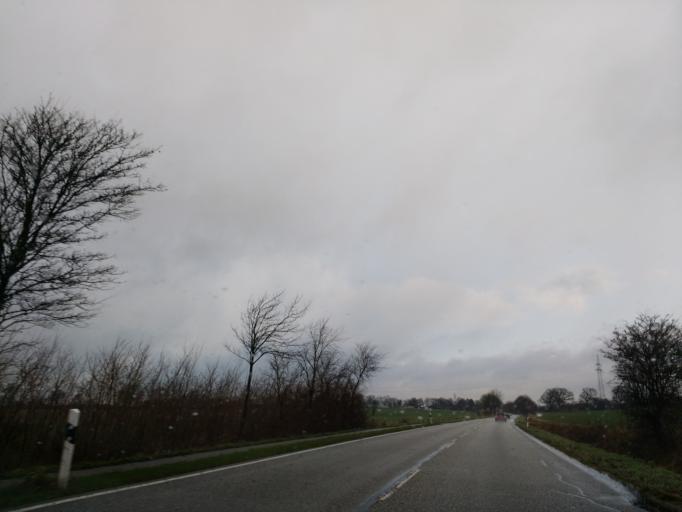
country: DE
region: Schleswig-Holstein
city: Goosefeld
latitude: 54.4218
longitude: 9.8028
